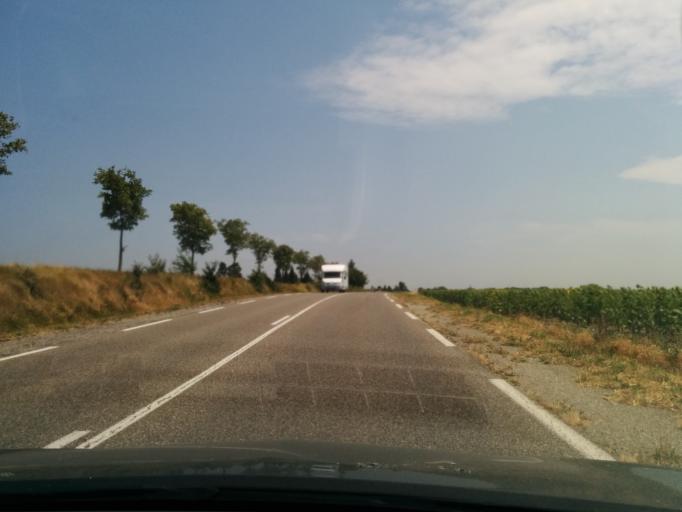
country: FR
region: Languedoc-Roussillon
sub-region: Departement de l'Aude
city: Villeneuve-la-Comptal
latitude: 43.3343
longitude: 1.9044
